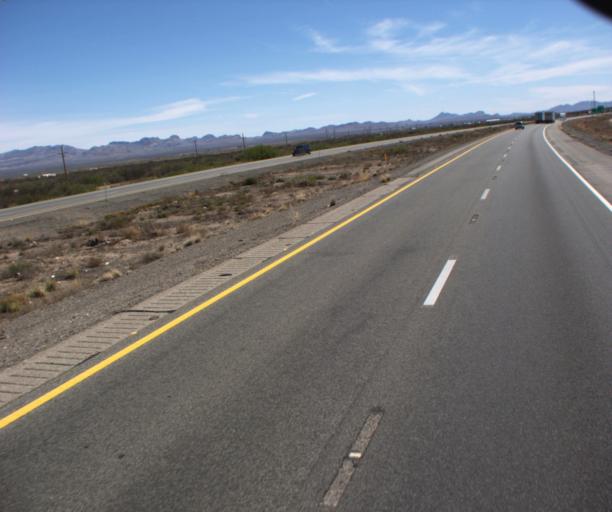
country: US
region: New Mexico
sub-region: Hidalgo County
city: Lordsburg
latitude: 32.2755
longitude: -109.2596
